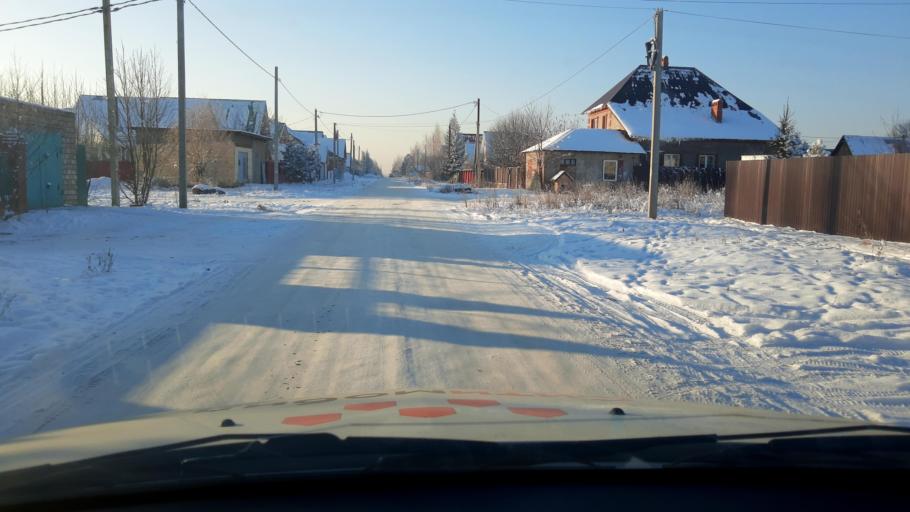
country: RU
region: Bashkortostan
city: Iglino
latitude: 54.7865
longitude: 56.2455
